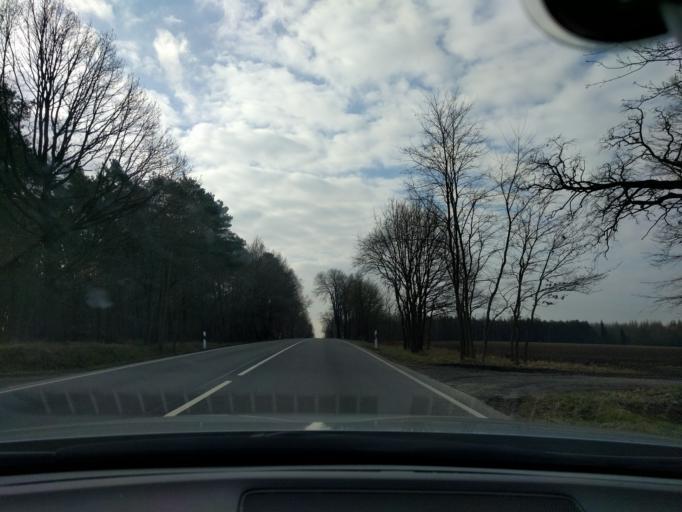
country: DE
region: Saxony-Anhalt
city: Colbitz
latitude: 52.3932
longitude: 11.6196
